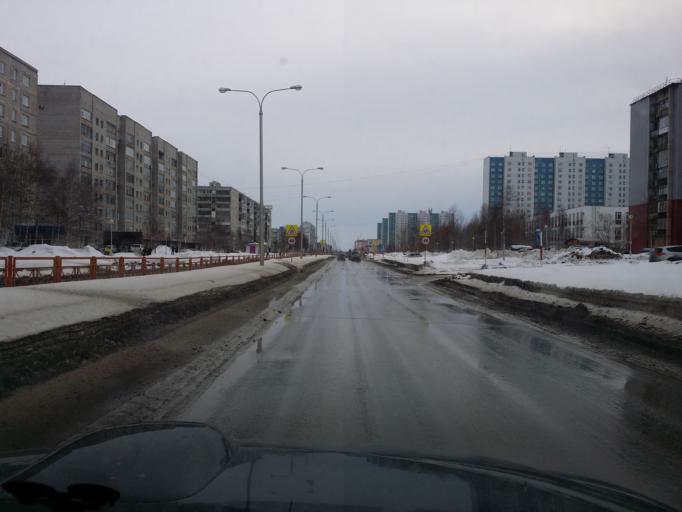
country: RU
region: Khanty-Mansiyskiy Avtonomnyy Okrug
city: Nizhnevartovsk
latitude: 60.9442
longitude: 76.6006
